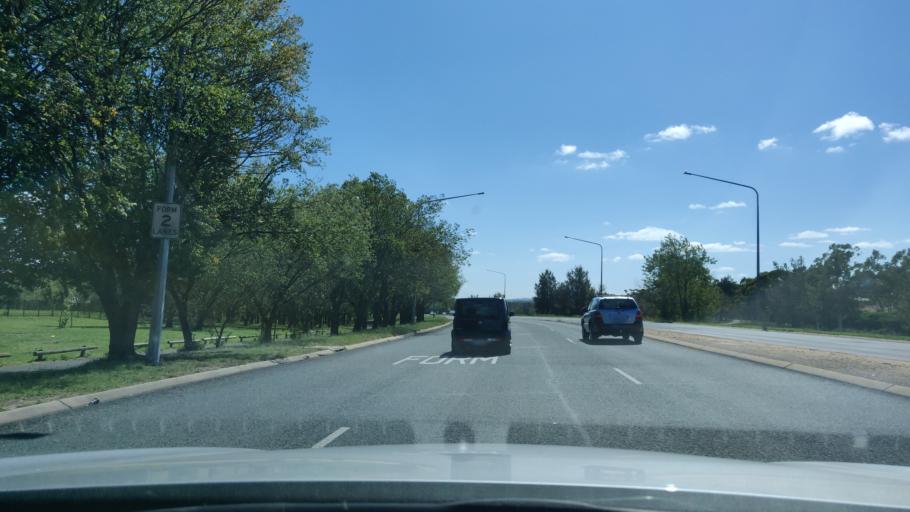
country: AU
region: Australian Capital Territory
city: Macarthur
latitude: -35.3630
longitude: 149.0923
